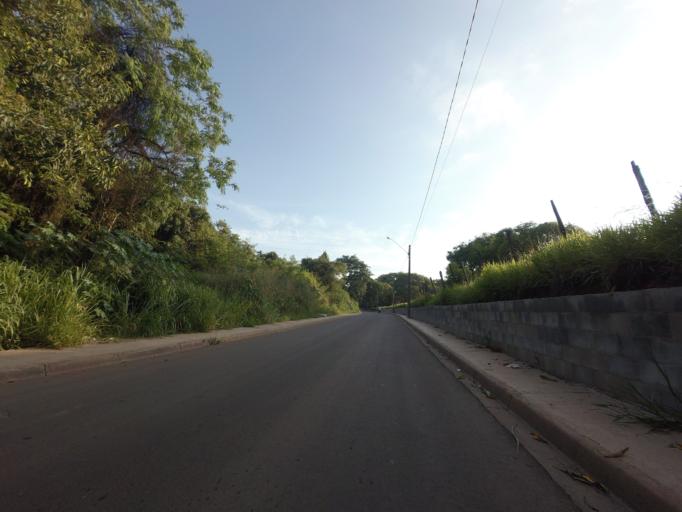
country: BR
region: Sao Paulo
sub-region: Piracicaba
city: Piracicaba
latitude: -22.7508
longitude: -47.6116
